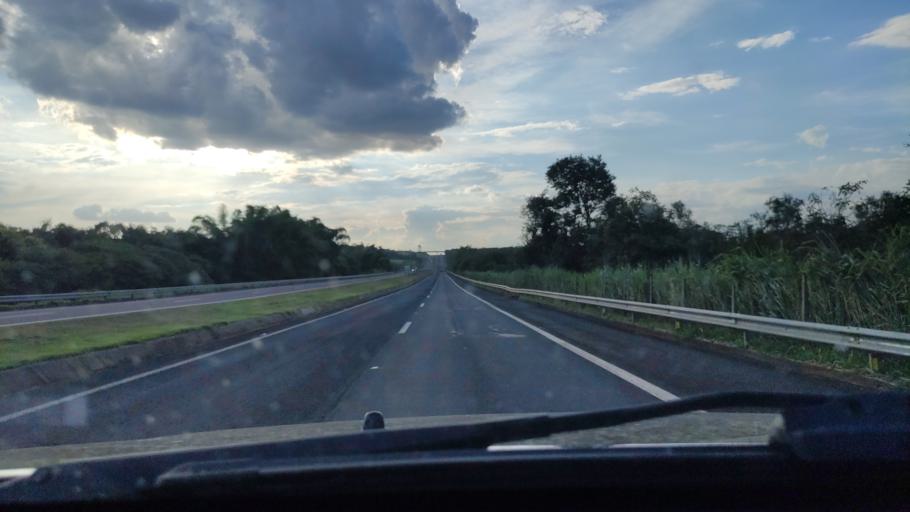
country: BR
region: Sao Paulo
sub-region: Rancharia
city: Rancharia
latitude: -22.4906
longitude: -50.9131
